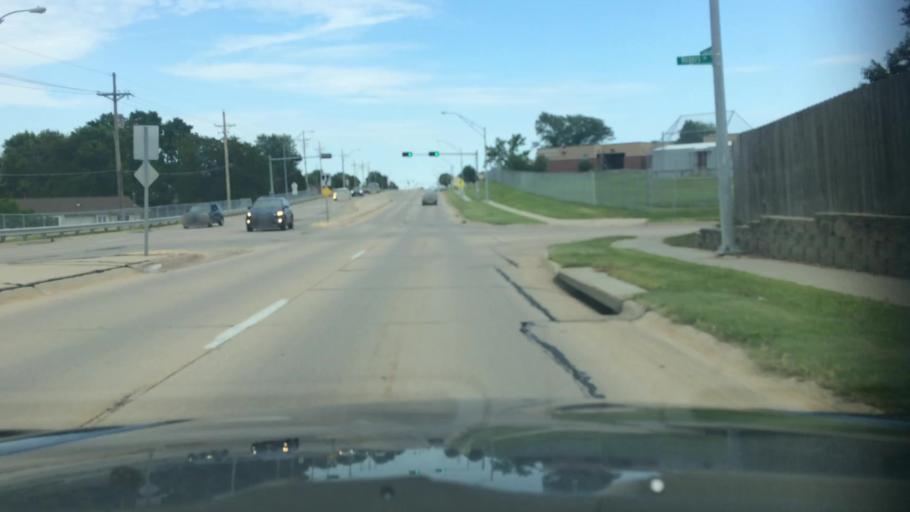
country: US
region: Nebraska
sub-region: Sarpy County
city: La Vista
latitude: 41.1762
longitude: -96.0336
